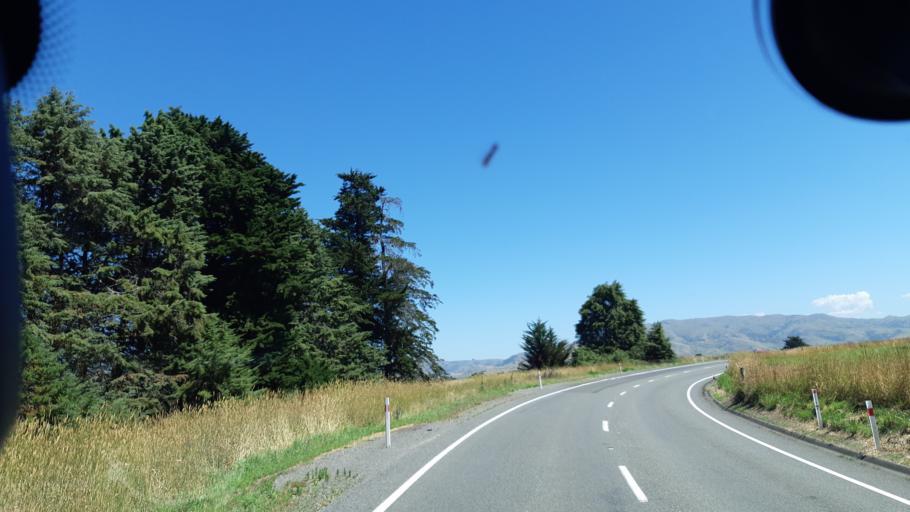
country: NZ
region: Canterbury
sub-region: Kaikoura District
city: Kaikoura
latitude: -42.7503
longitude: 173.2692
